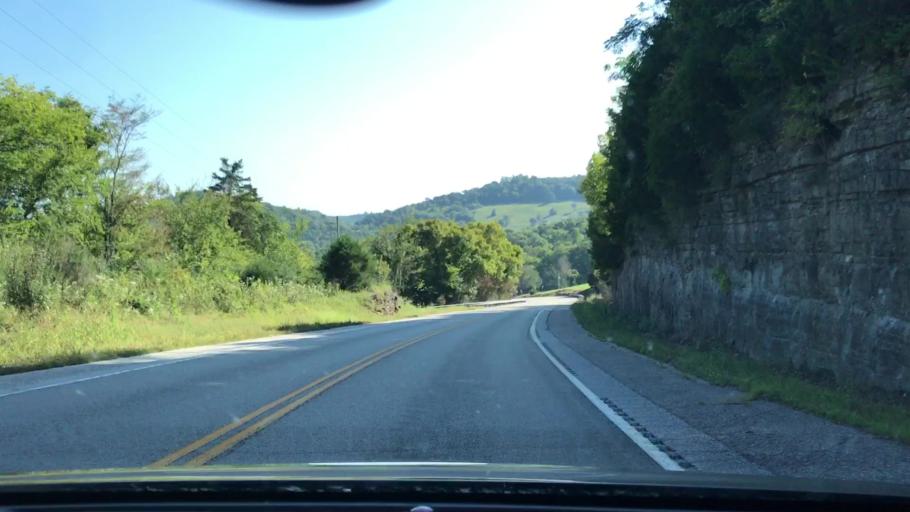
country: US
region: Tennessee
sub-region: Jackson County
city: Gainesboro
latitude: 36.3559
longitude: -85.7858
